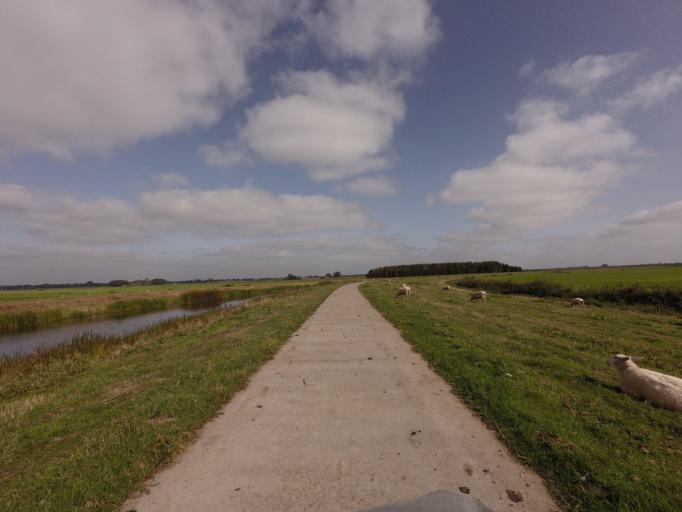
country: NL
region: Overijssel
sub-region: Gemeente Steenwijkerland
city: Steenwijk
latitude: 52.8114
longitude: 6.1624
